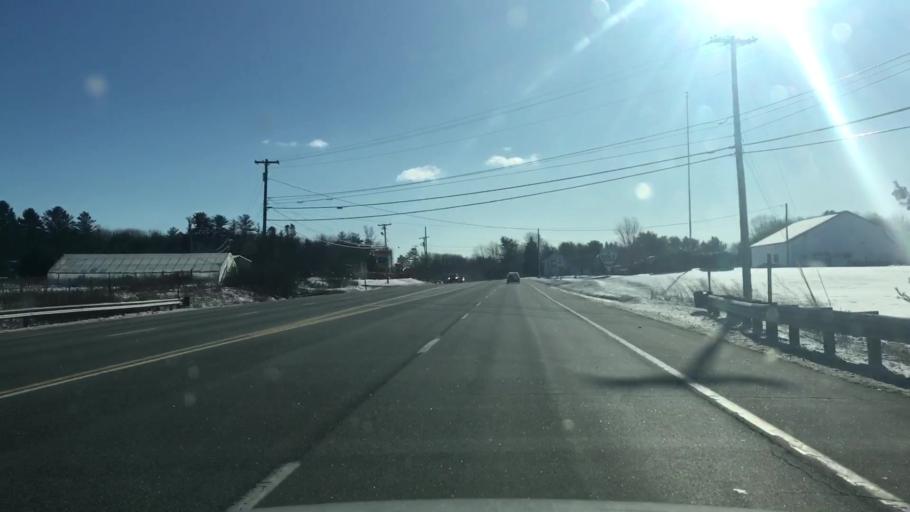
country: US
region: Maine
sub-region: Androscoggin County
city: Auburn
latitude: 44.1625
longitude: -70.2337
